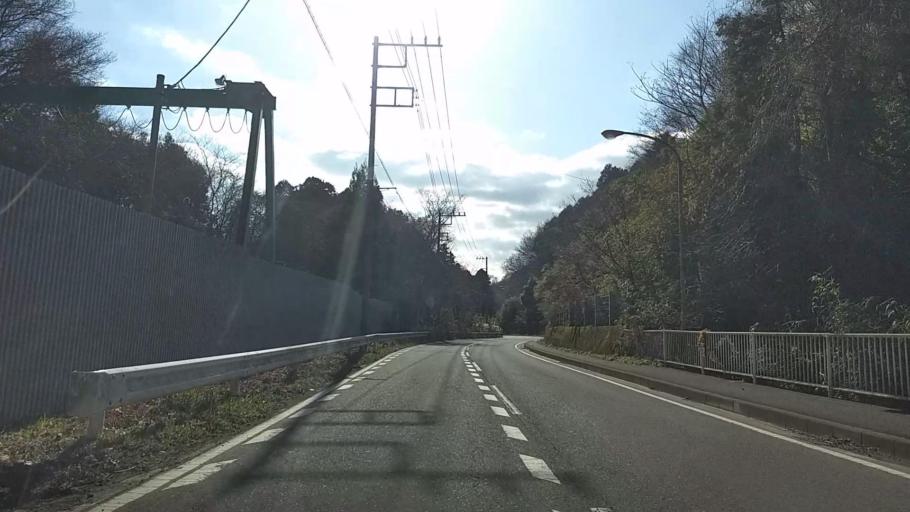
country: JP
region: Kanagawa
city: Atsugi
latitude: 35.4627
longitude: 139.2904
